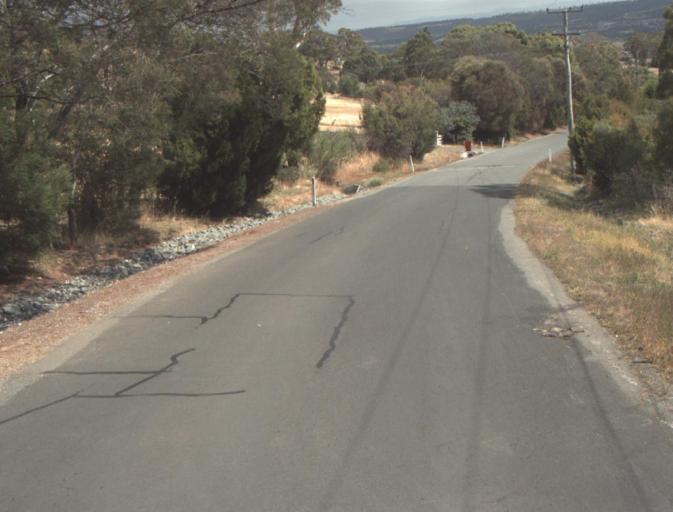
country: AU
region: Tasmania
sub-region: Launceston
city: Newstead
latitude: -41.4470
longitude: 147.2111
